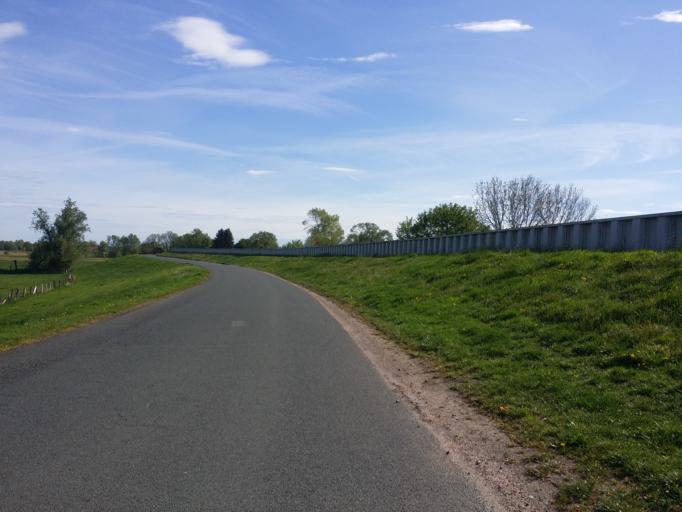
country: DE
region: Lower Saxony
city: Lemwerder
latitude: 53.1545
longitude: 8.6293
